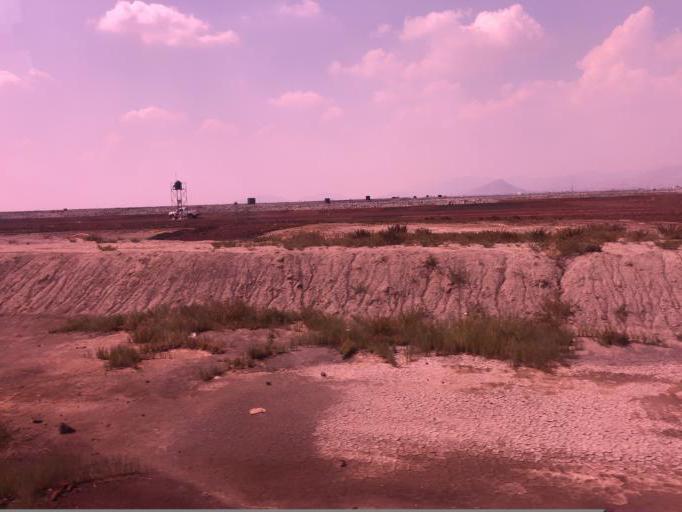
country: MX
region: Mexico
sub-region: Atenco
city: Colonia el Salado
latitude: 19.5454
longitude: -98.9849
